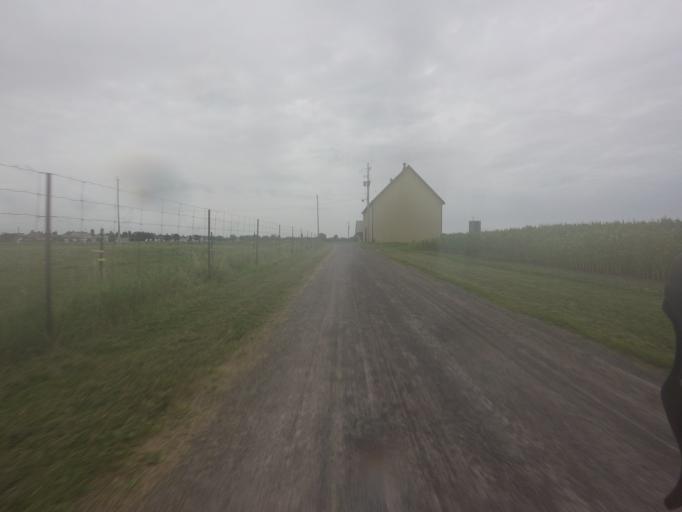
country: CA
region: Ontario
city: Ottawa
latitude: 45.3817
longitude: -75.7135
